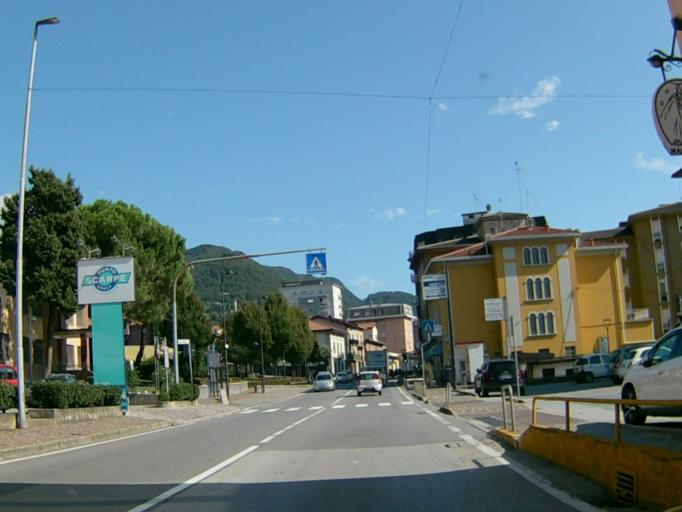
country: IT
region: Lombardy
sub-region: Provincia di Lecco
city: Vercurago
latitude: 45.8024
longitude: 9.4294
